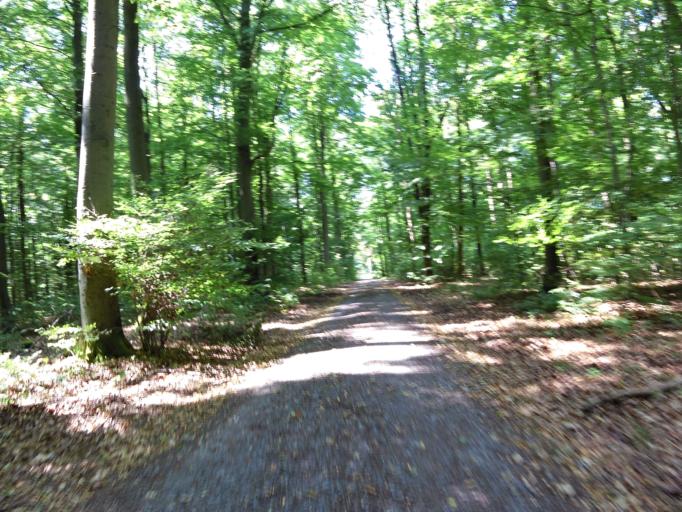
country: DE
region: Bavaria
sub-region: Regierungsbezirk Unterfranken
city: Wuerzburg
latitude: 49.7629
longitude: 9.8785
